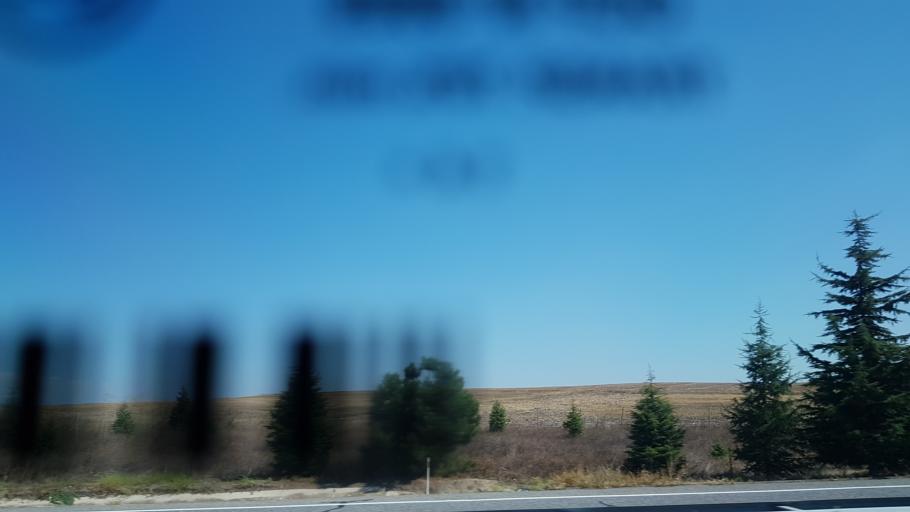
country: TR
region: Kirklareli
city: Luleburgaz
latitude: 41.4085
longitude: 27.3866
